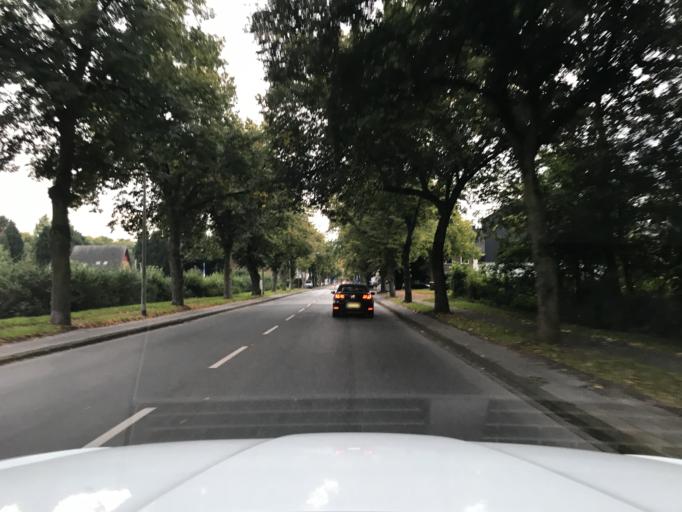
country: DE
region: North Rhine-Westphalia
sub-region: Regierungsbezirk Dusseldorf
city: Hochfeld
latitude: 51.3867
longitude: 6.7832
